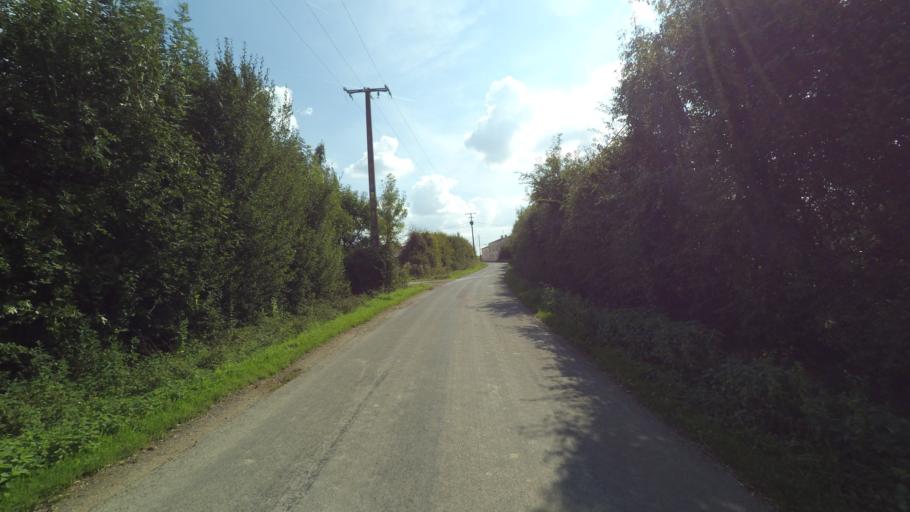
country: FR
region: Pays de la Loire
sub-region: Departement de la Vendee
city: Bouffere
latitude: 46.9597
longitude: -1.3803
